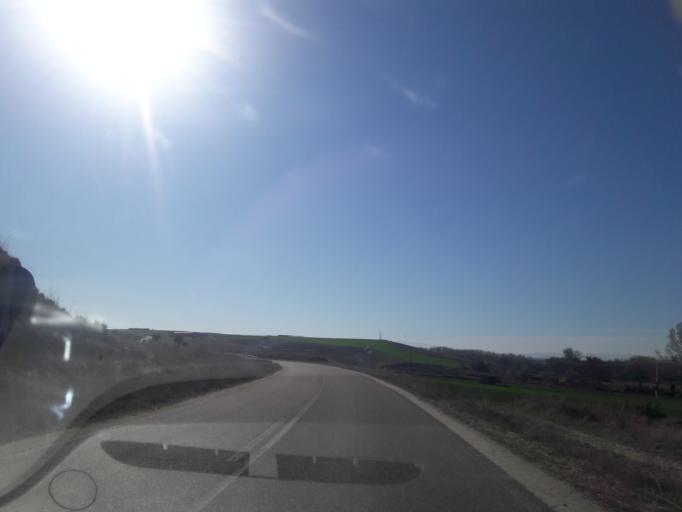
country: ES
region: Castille and Leon
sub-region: Provincia de Salamanca
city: Tordillos
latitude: 40.8550
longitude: -5.3470
